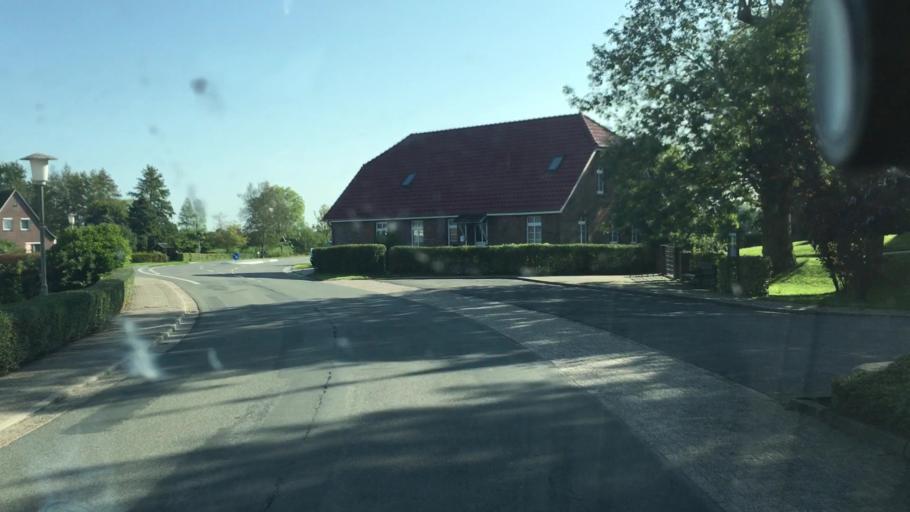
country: DE
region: Lower Saxony
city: Jever
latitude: 53.6344
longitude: 7.8427
